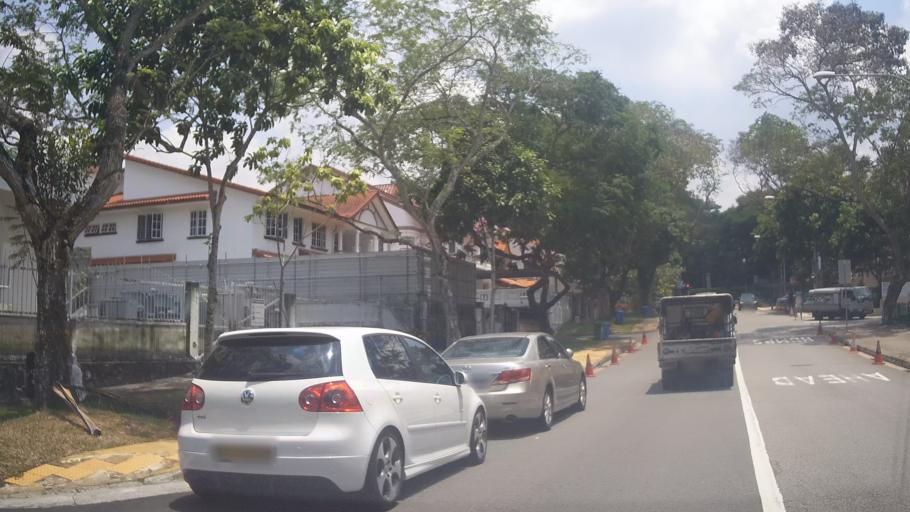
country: SG
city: Singapore
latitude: 1.3169
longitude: 103.7835
